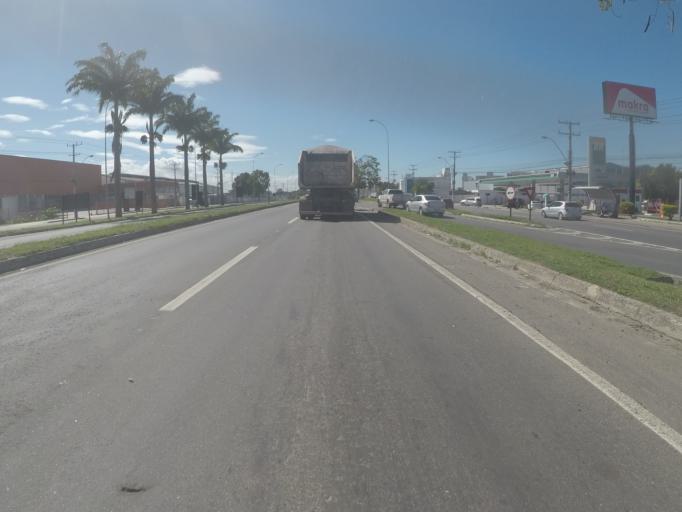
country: BR
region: Espirito Santo
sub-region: Serra
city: Serra
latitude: -20.2052
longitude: -40.2692
